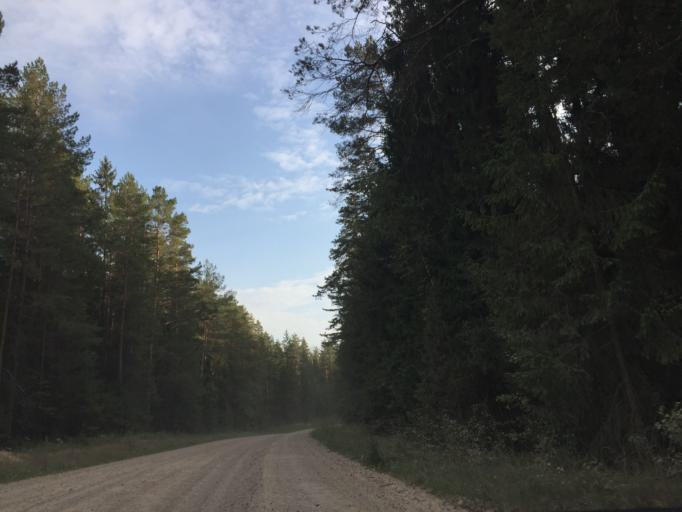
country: LV
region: Baldone
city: Baldone
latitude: 56.7888
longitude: 24.4428
